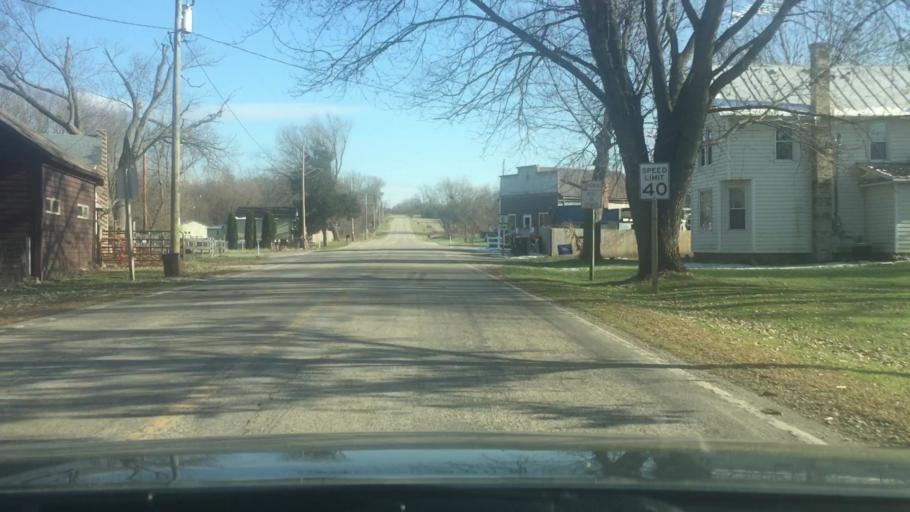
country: US
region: Wisconsin
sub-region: Jefferson County
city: Palmyra
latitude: 42.9365
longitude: -88.5873
